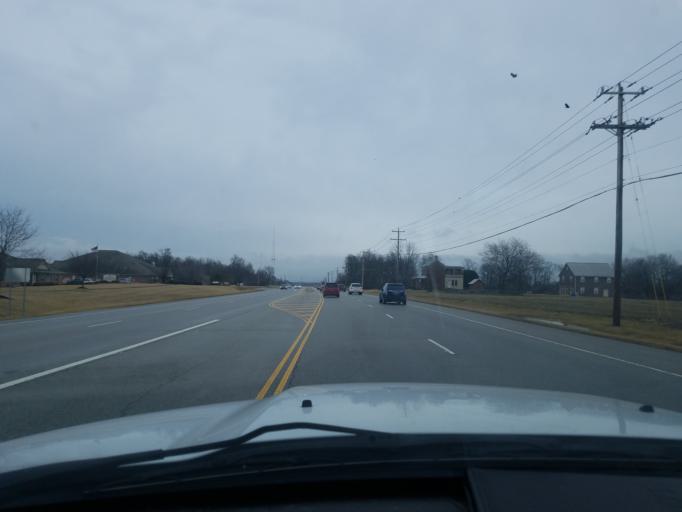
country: US
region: Ohio
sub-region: Butler County
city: Wetherington
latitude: 39.3517
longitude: -84.3470
